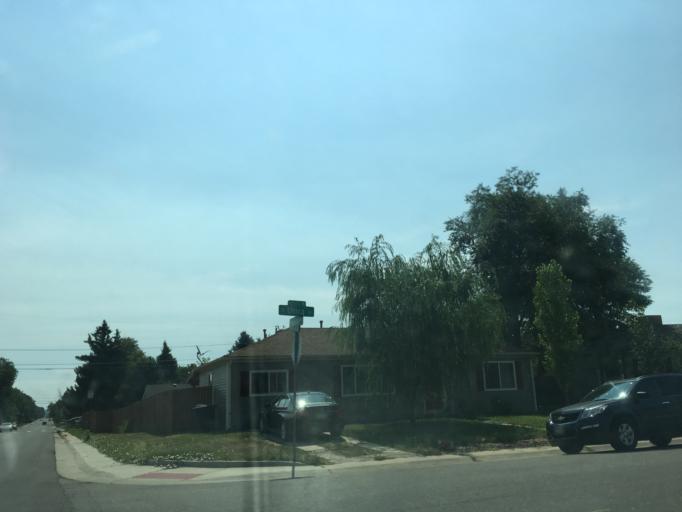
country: US
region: Colorado
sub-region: Jefferson County
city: Lakewood
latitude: 39.6931
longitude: -105.0450
